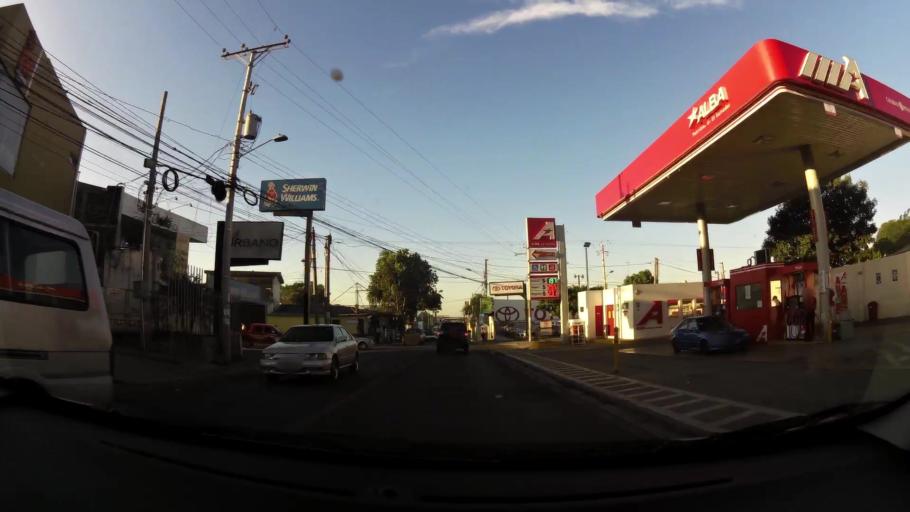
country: SV
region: Sonsonate
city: Sonsonate
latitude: 13.7202
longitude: -89.7208
